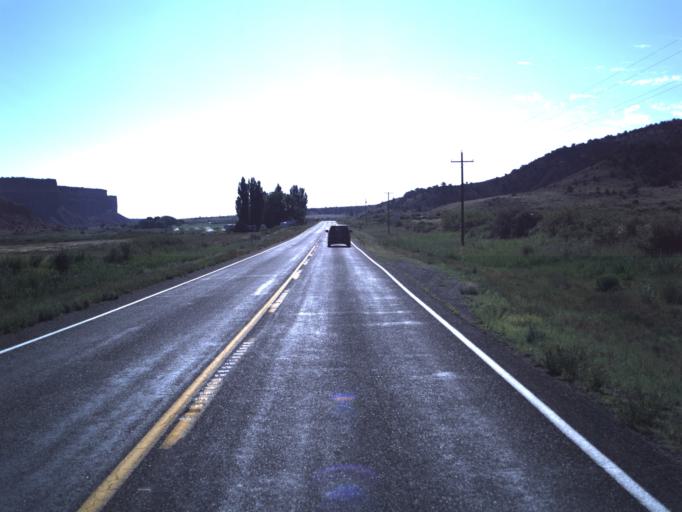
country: US
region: Utah
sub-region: Wayne County
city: Loa
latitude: 38.3067
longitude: -111.5061
